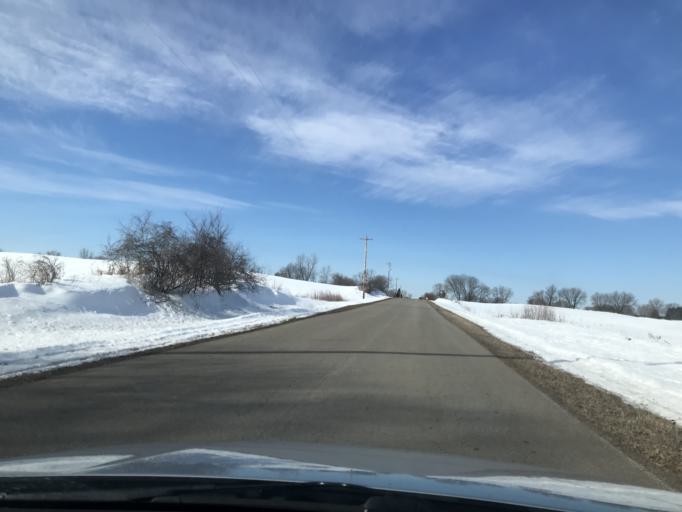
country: US
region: Wisconsin
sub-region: Oconto County
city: Gillett
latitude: 44.9692
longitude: -88.3189
